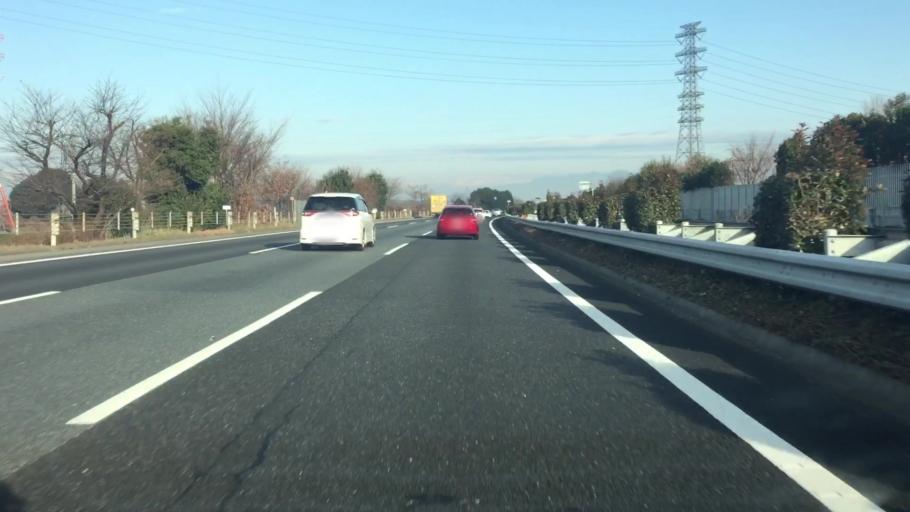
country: JP
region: Saitama
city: Honjo
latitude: 36.1785
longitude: 139.1913
